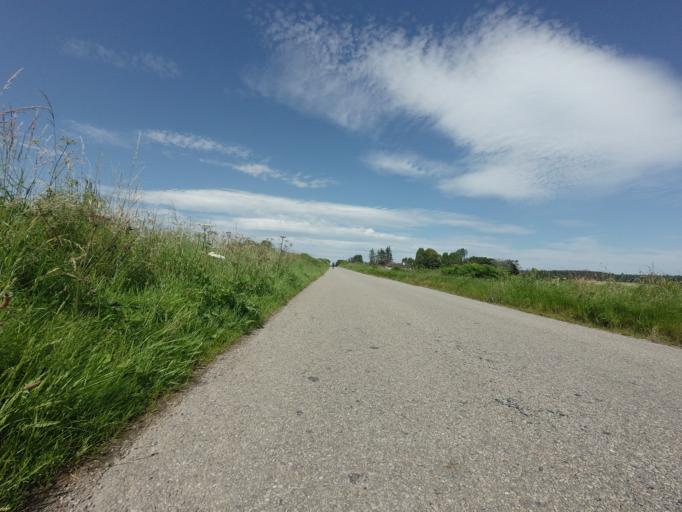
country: GB
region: Scotland
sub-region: Highland
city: Inverness
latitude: 57.5245
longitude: -4.3153
